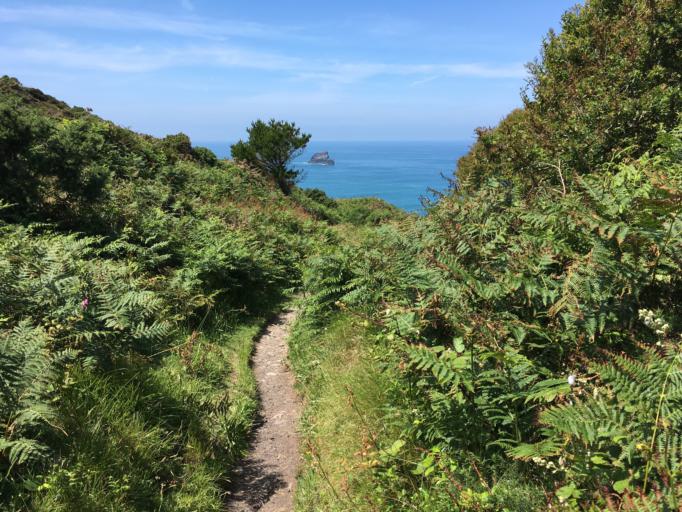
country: GB
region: England
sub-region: Cornwall
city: Saint Agnes
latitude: 50.3204
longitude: -5.2121
